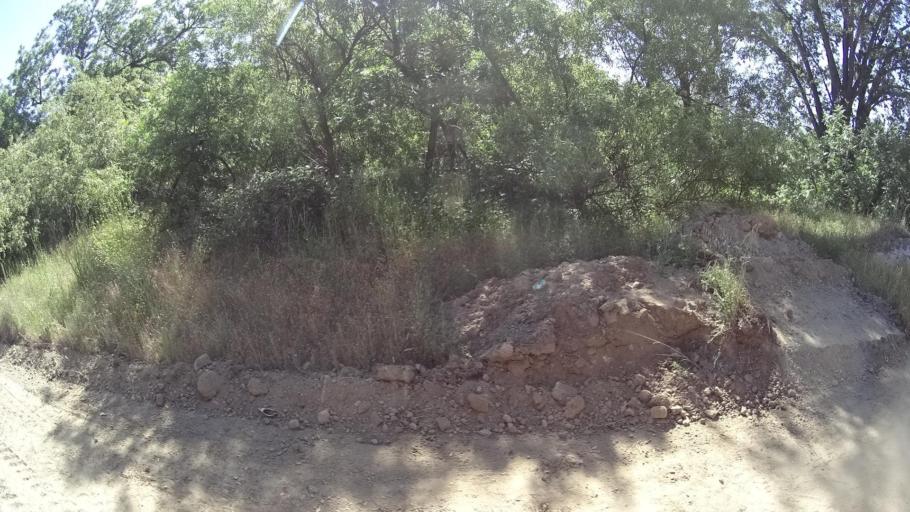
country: US
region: California
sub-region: Lake County
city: Clearlake
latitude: 39.0352
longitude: -122.5738
